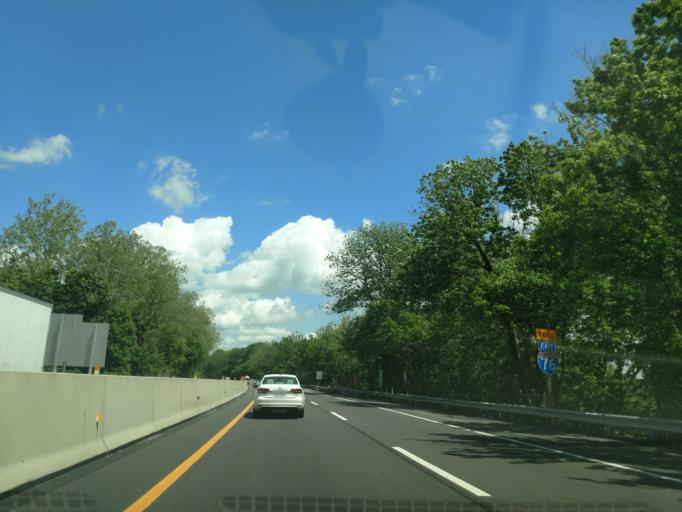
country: US
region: Pennsylvania
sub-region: Chester County
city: Malvern
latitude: 40.0736
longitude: -75.5239
